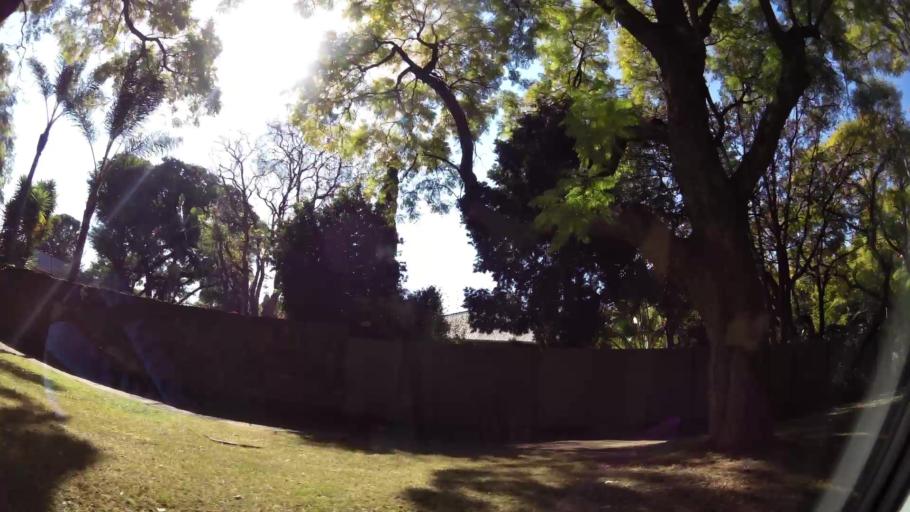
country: ZA
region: Gauteng
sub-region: City of Tshwane Metropolitan Municipality
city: Pretoria
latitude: -25.7663
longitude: 28.2462
